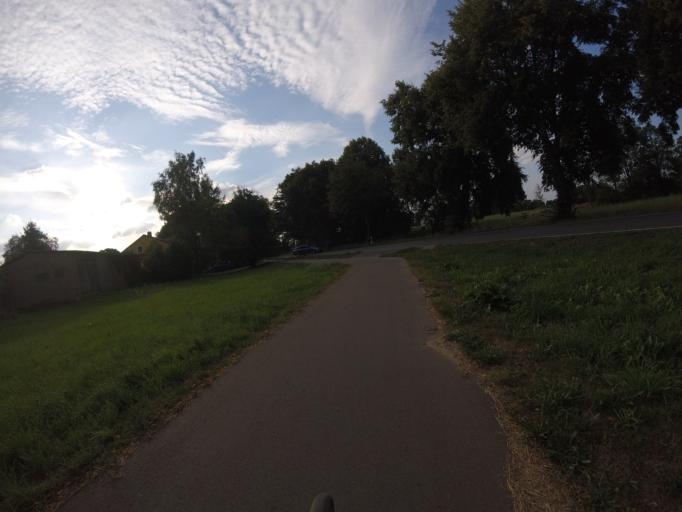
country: DE
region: Brandenburg
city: Altlandsberg
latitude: 52.5709
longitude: 13.7183
